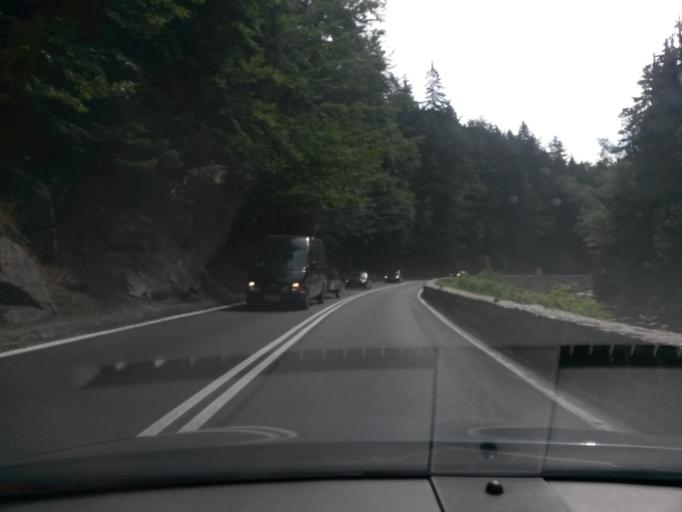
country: PL
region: Lower Silesian Voivodeship
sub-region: Powiat jeleniogorski
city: Szklarska Poreba
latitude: 50.8294
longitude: 15.5357
